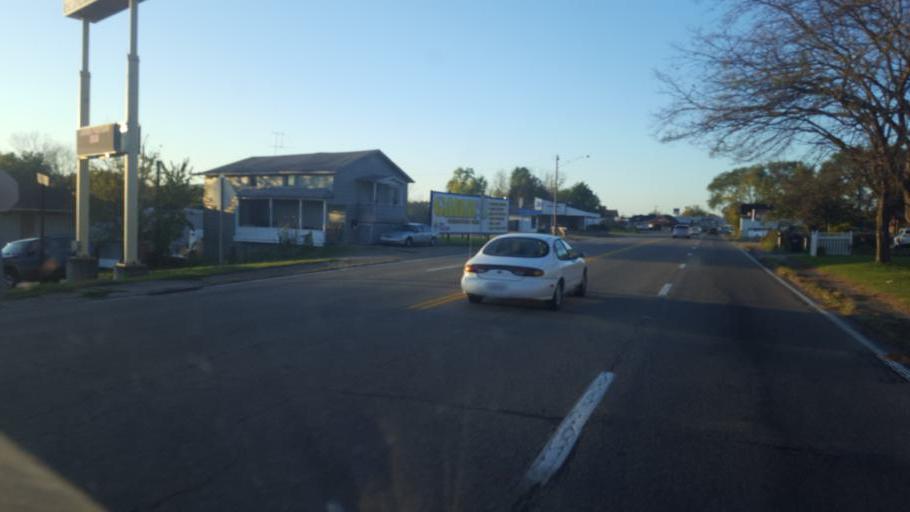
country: US
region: Ohio
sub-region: Scioto County
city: Lucasville
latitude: 38.8757
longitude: -82.9962
